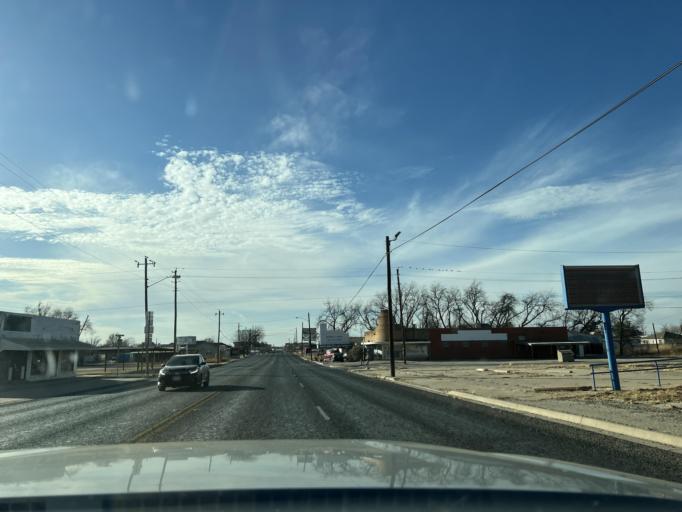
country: US
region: Texas
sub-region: Scurry County
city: Snyder
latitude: 32.7170
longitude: -100.9083
